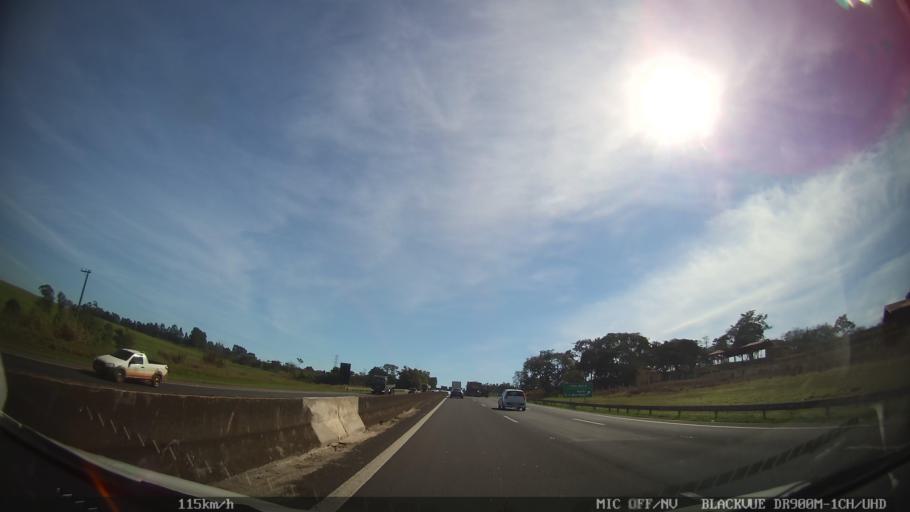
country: BR
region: Sao Paulo
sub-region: Pirassununga
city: Pirassununga
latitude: -22.0430
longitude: -47.4311
